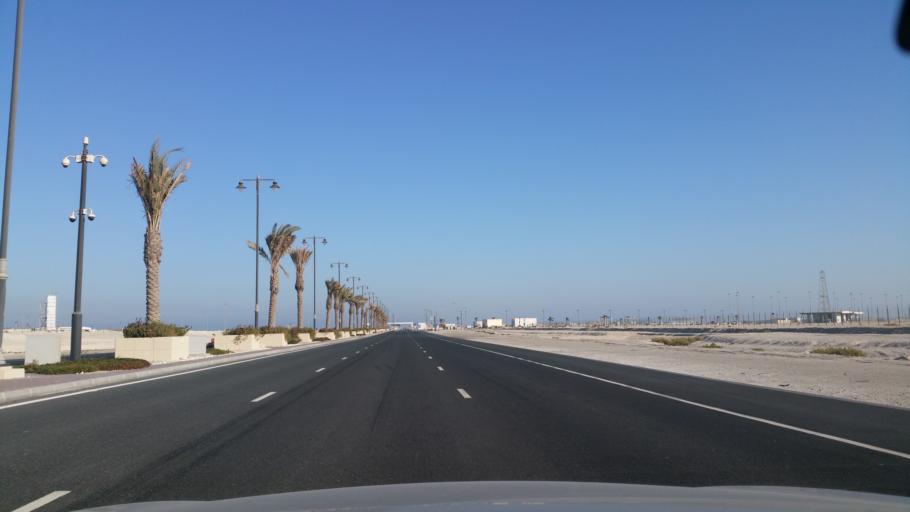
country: QA
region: Al Wakrah
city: Umm Sa'id
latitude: 25.0565
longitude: 51.5975
